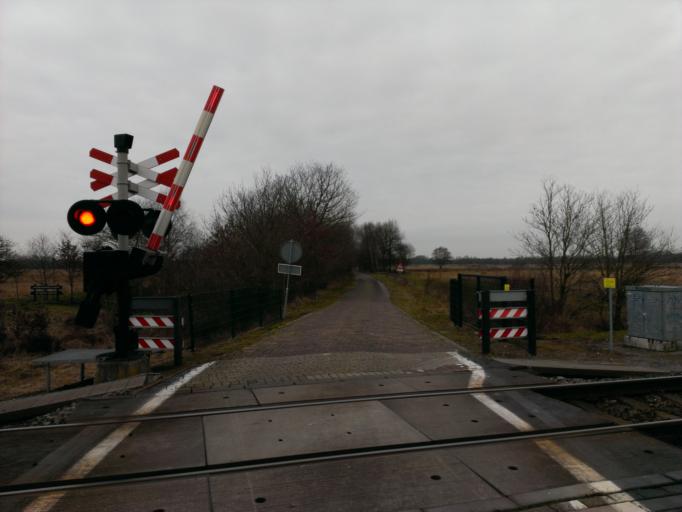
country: NL
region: Drenthe
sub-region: Gemeente Hoogeveen
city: Hoogeveen
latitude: 52.7580
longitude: 6.4863
